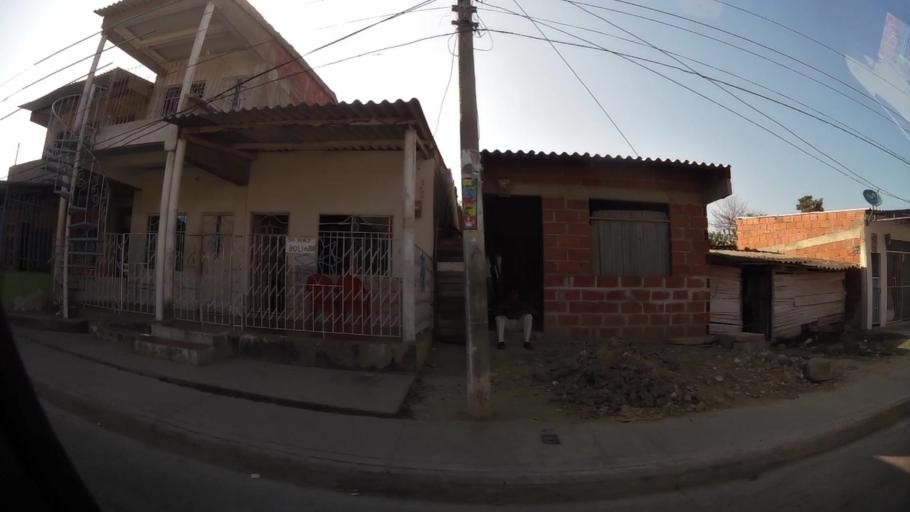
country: CO
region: Bolivar
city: Cartagena
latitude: 10.4126
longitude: -75.4999
